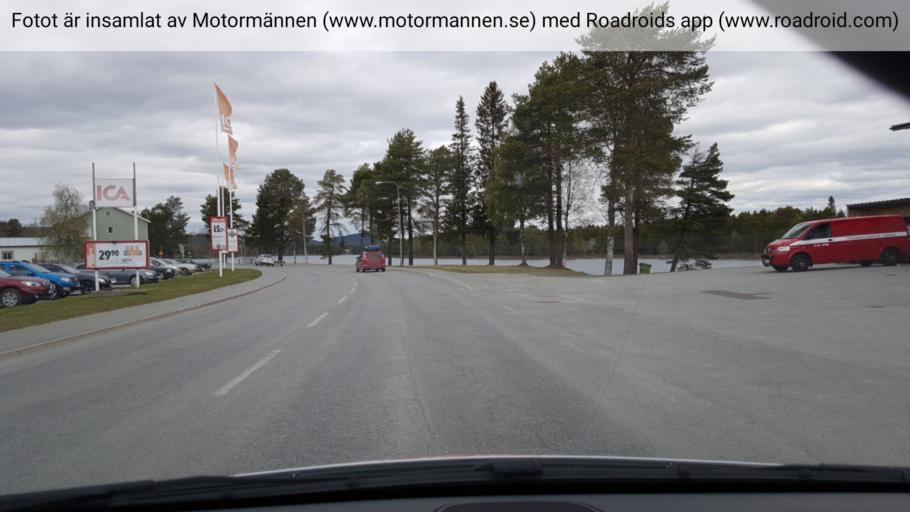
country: SE
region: Vaesterbotten
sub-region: Sorsele Kommun
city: Sorsele
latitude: 65.5364
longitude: 17.5317
